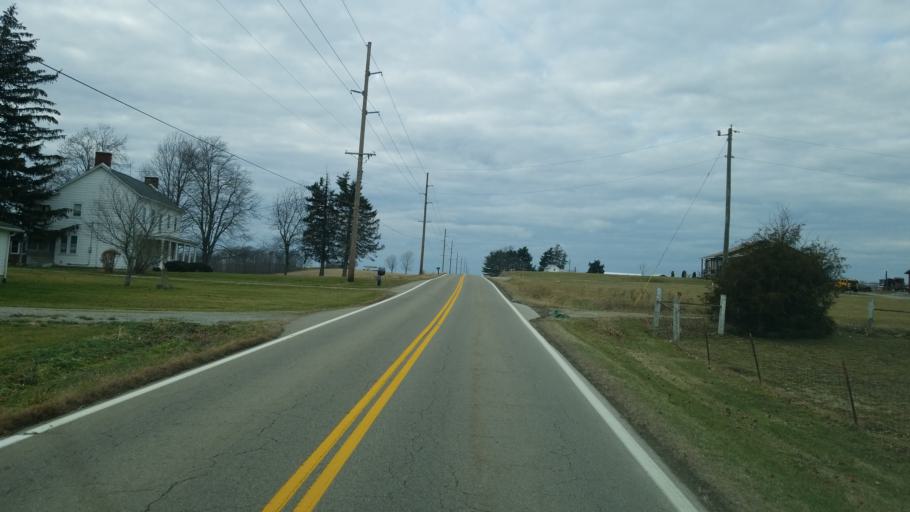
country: US
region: Ohio
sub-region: Ross County
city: Frankfort
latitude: 39.3544
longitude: -83.2512
